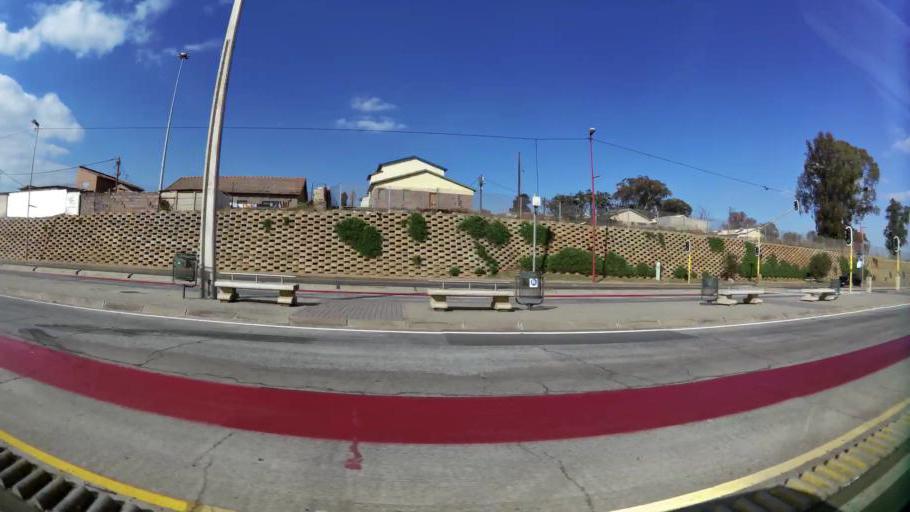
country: ZA
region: Gauteng
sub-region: City of Johannesburg Metropolitan Municipality
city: Soweto
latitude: -26.2592
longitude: 27.8912
